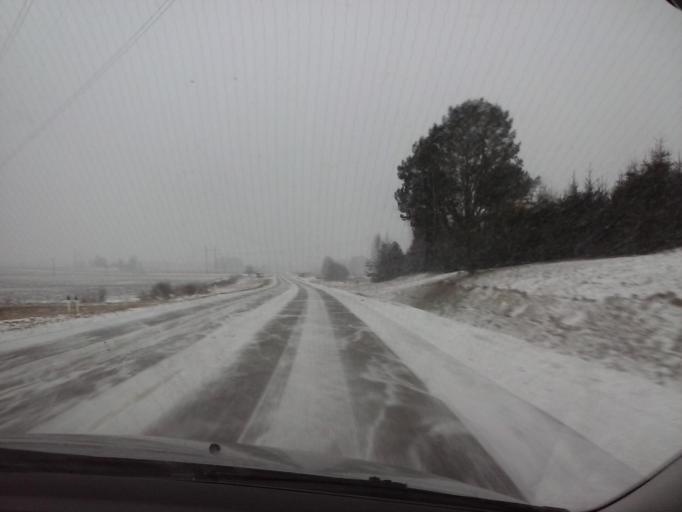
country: EE
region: Valgamaa
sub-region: Torva linn
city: Torva
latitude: 58.0330
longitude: 26.1775
